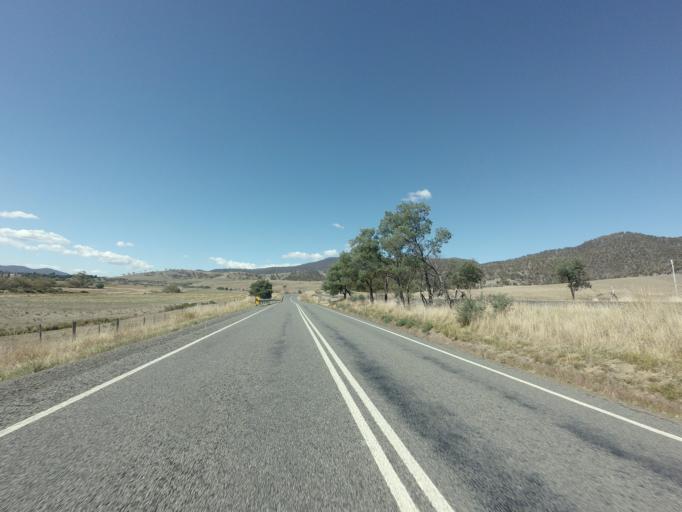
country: AU
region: Tasmania
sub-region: Northern Midlands
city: Evandale
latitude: -41.7352
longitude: 147.8115
